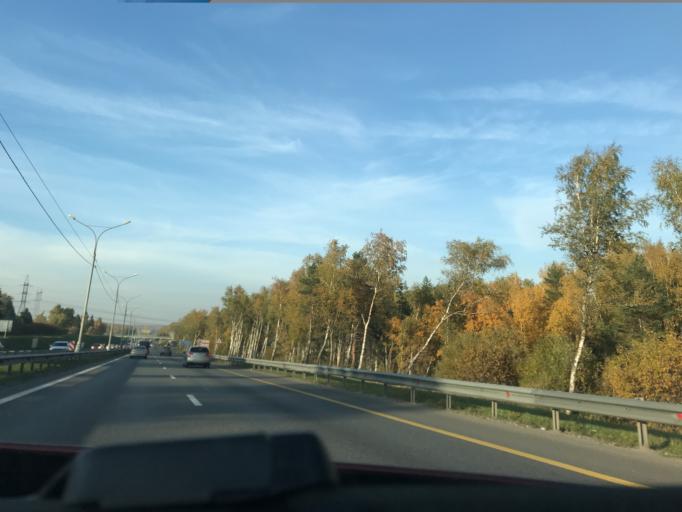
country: RU
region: Moskovskaya
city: Gorki-Leninskiye
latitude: 55.4758
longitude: 37.8527
